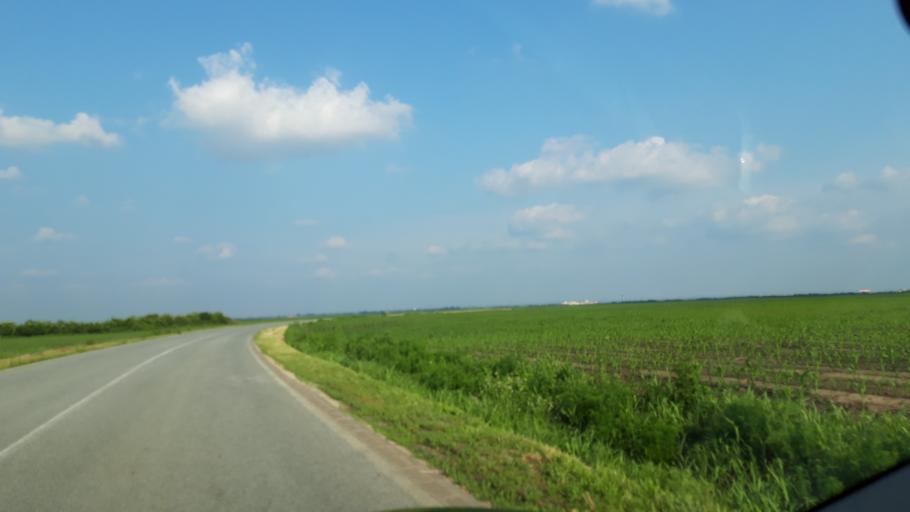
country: RS
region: Autonomna Pokrajina Vojvodina
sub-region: Sremski Okrug
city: Ingija
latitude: 45.0881
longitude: 20.1058
